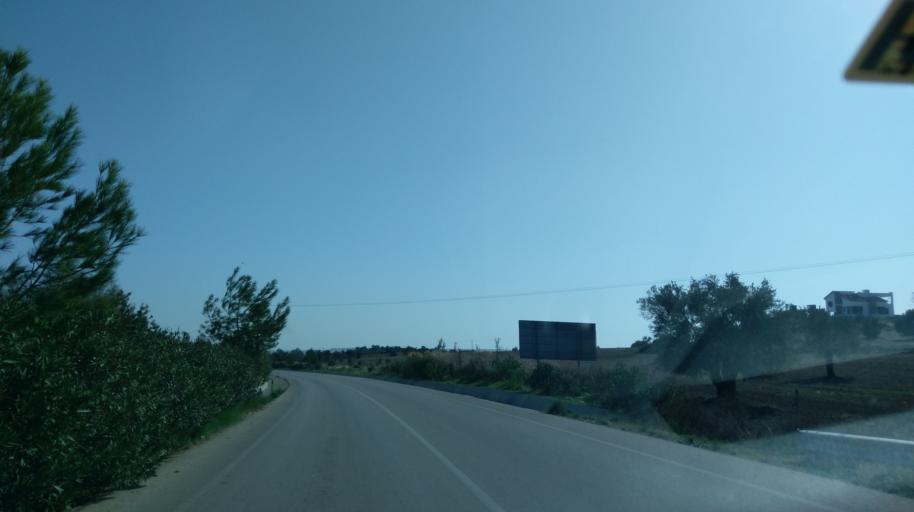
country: CY
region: Ammochostos
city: Trikomo
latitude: 35.4039
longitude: 33.9925
